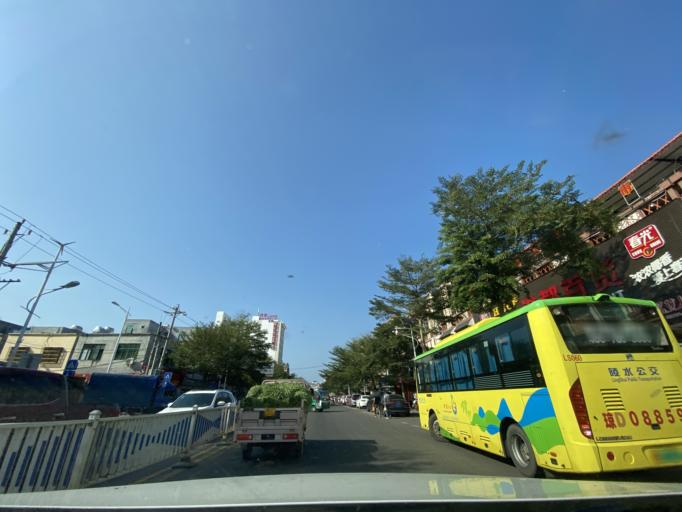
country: CN
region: Hainan
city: Yingzhou
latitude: 18.4237
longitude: 109.8552
